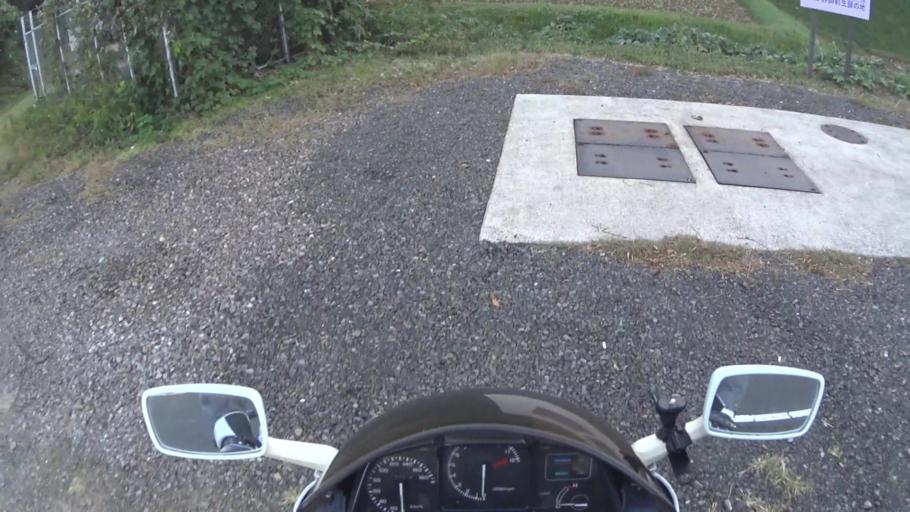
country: JP
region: Hyogo
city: Toyooka
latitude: 35.6892
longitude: 134.9914
